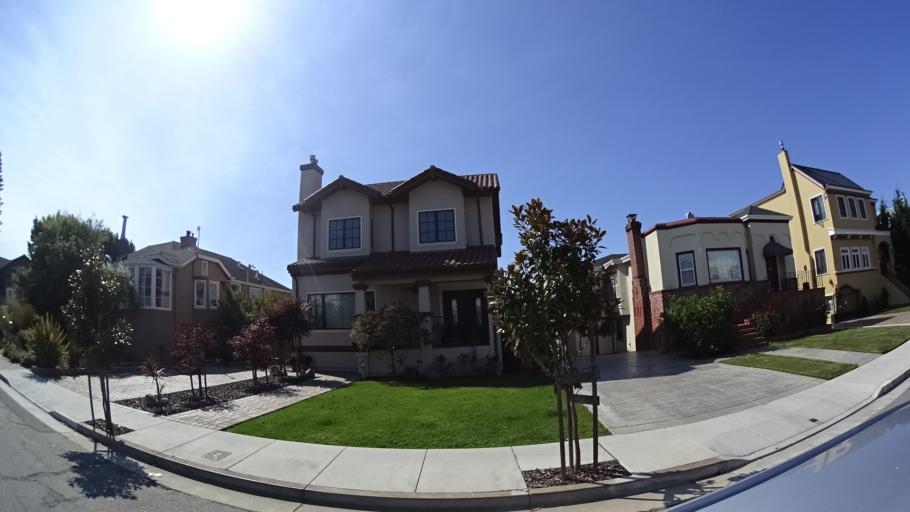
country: US
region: California
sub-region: San Mateo County
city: Daly City
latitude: 37.7246
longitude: -122.4653
